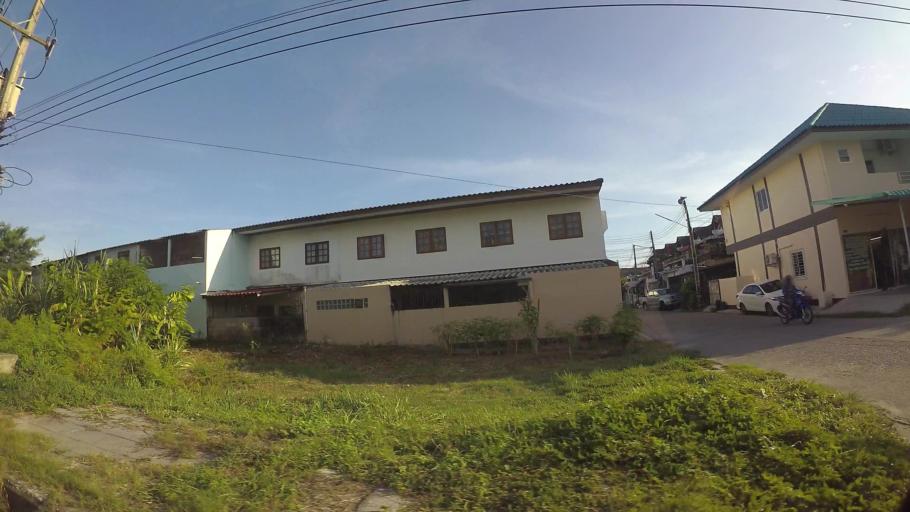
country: TH
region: Rayong
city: Rayong
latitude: 12.6811
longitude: 101.2917
